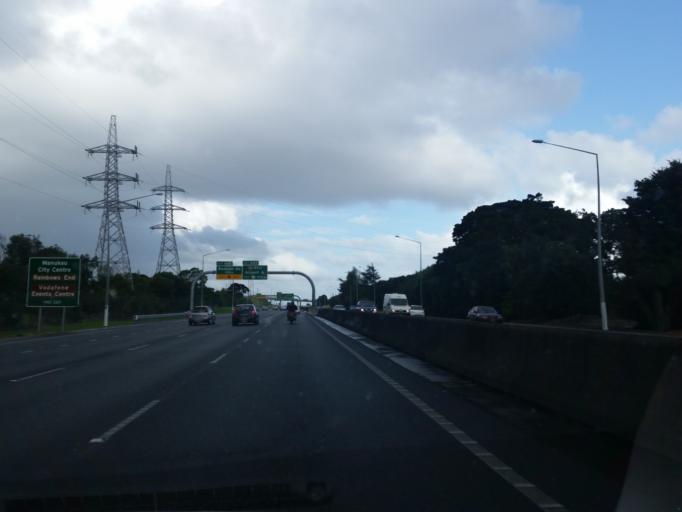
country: NZ
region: Auckland
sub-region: Auckland
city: Manukau City
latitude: -36.9861
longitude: 174.8848
